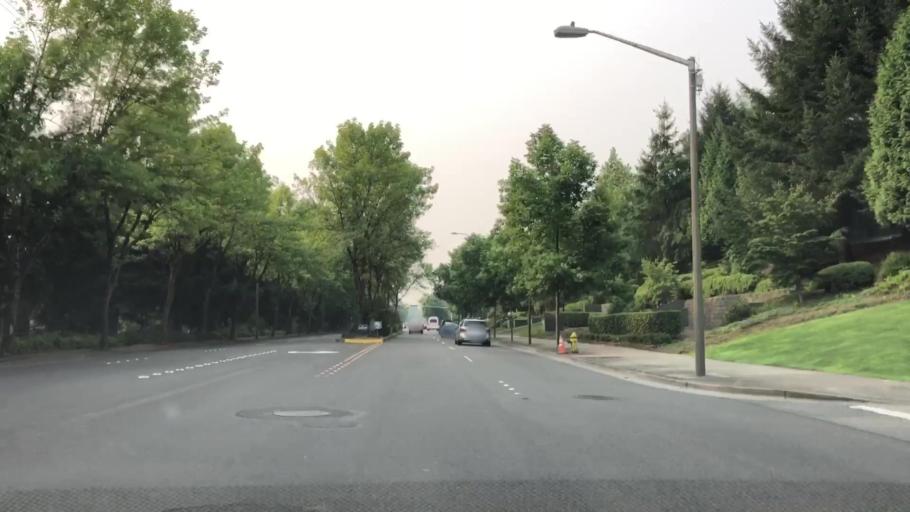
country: US
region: Washington
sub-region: King County
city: Redmond
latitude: 47.6517
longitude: -122.1325
